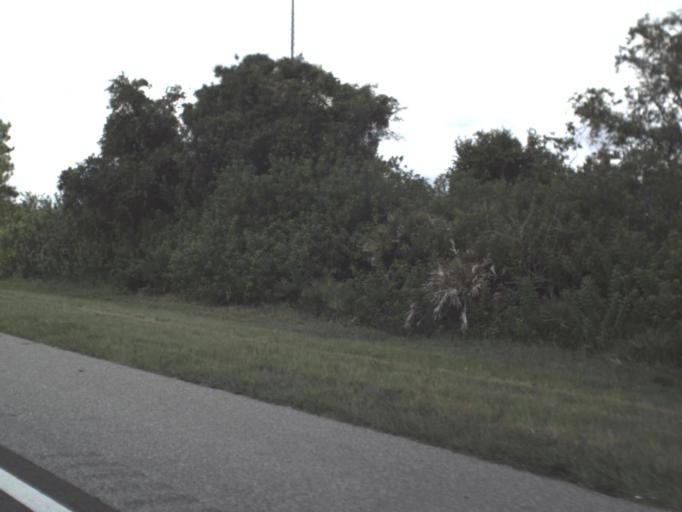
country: US
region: Florida
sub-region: Hillsborough County
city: Apollo Beach
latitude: 27.7441
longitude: -82.3820
